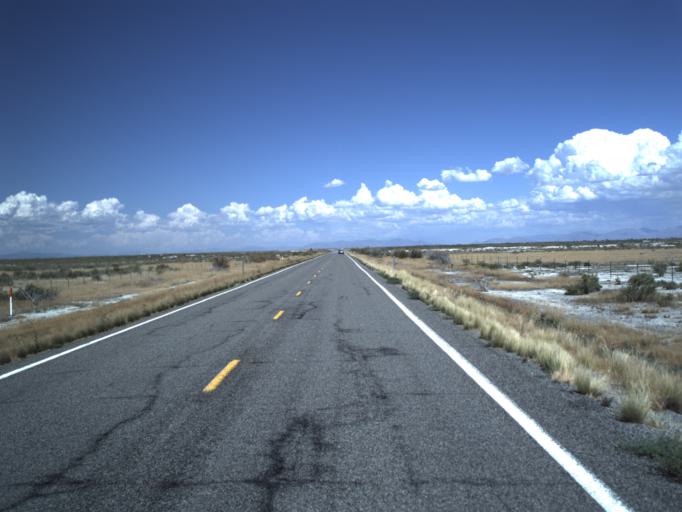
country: US
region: Utah
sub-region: Millard County
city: Delta
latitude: 39.2970
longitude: -112.8171
